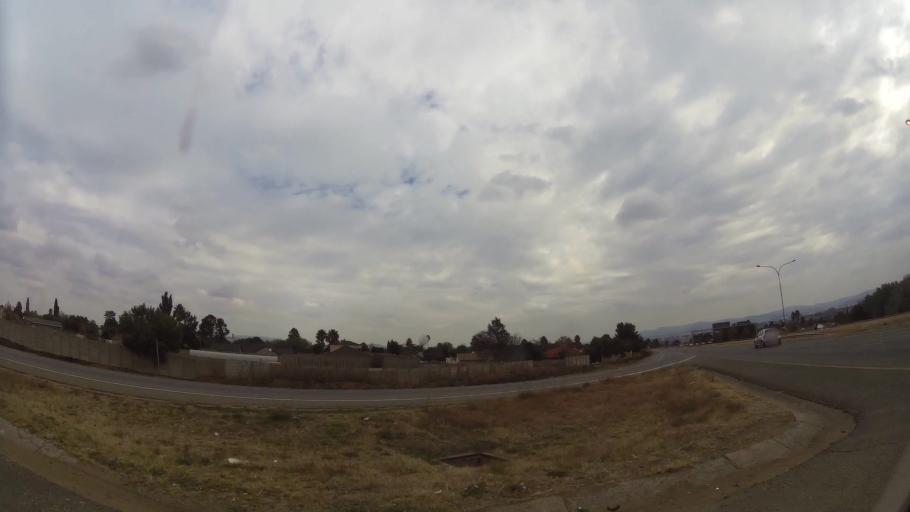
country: ZA
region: Gauteng
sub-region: Ekurhuleni Metropolitan Municipality
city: Germiston
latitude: -26.3506
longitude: 28.0974
